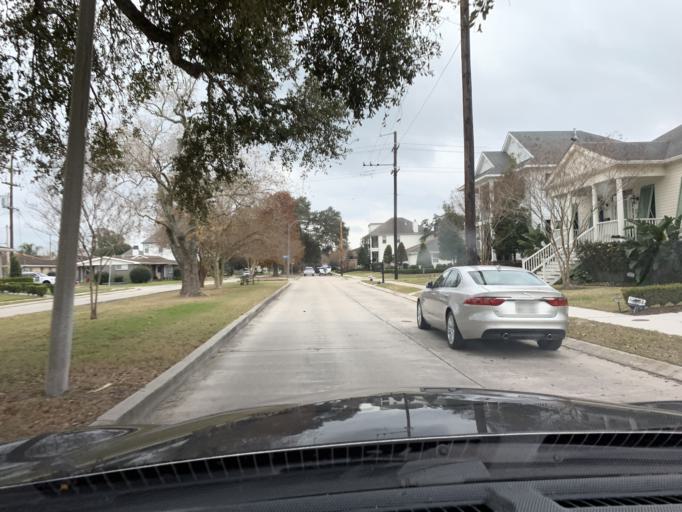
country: US
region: Louisiana
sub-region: Jefferson Parish
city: Metairie
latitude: 30.0159
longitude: -90.1014
